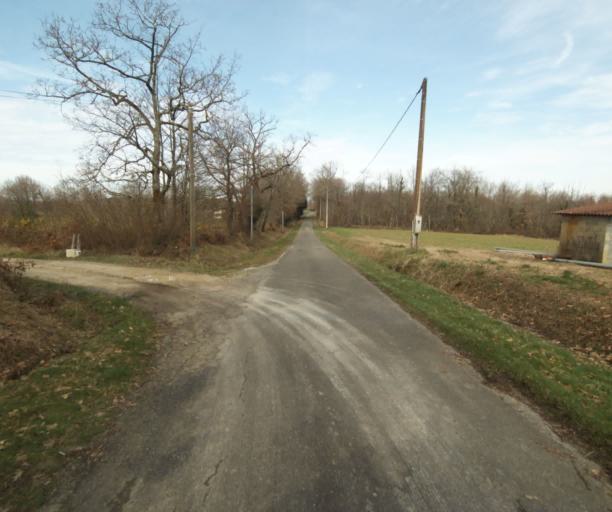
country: FR
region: Midi-Pyrenees
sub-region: Departement du Gers
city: Eauze
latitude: 43.9065
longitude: 0.0357
